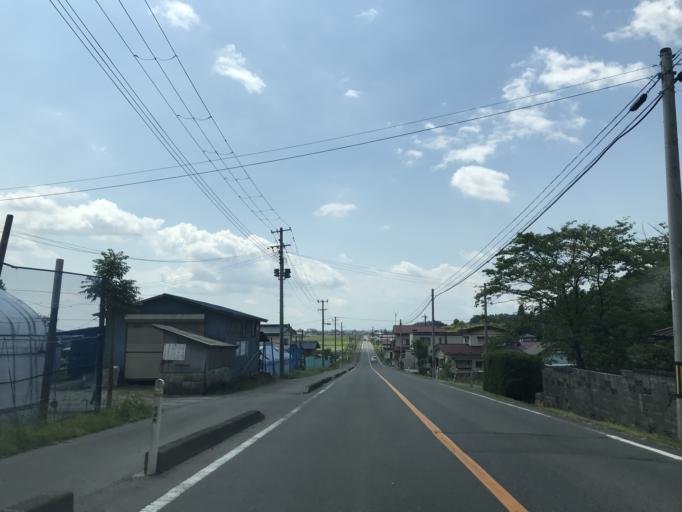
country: JP
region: Miyagi
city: Kogota
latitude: 38.6183
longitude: 141.0188
